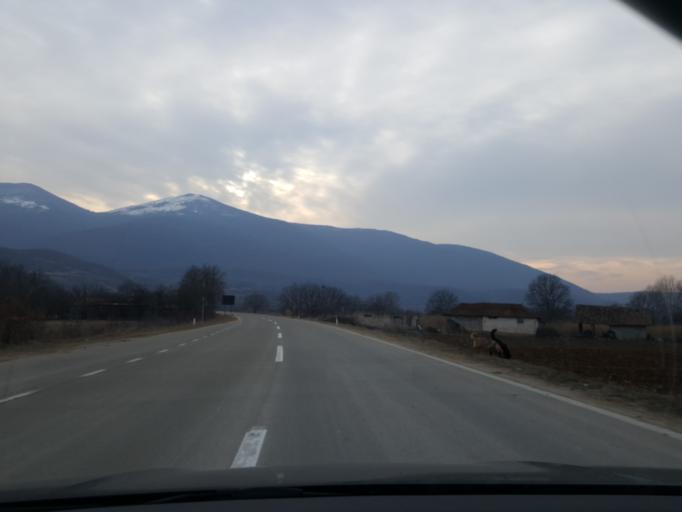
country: RS
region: Central Serbia
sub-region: Pirotski Okrug
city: Bela Palanka
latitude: 43.2292
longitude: 22.3143
